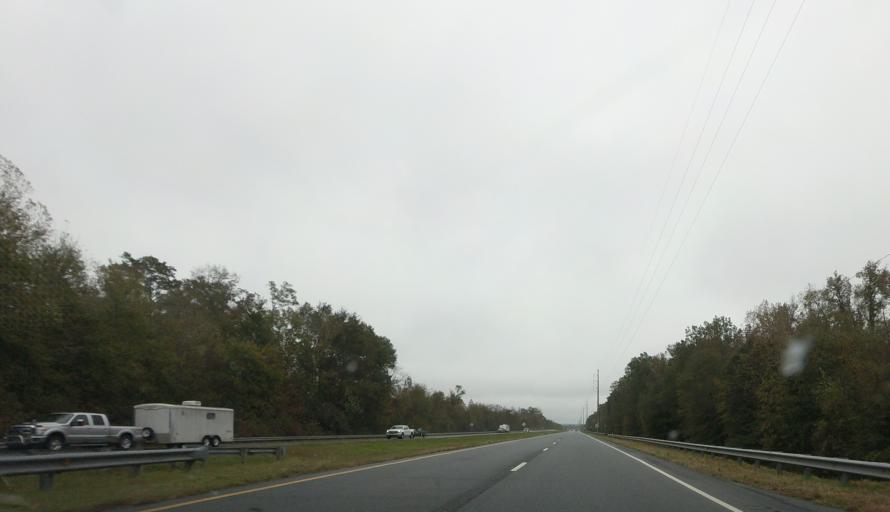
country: US
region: Georgia
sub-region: Taylor County
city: Reynolds
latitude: 32.5495
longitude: -84.0460
